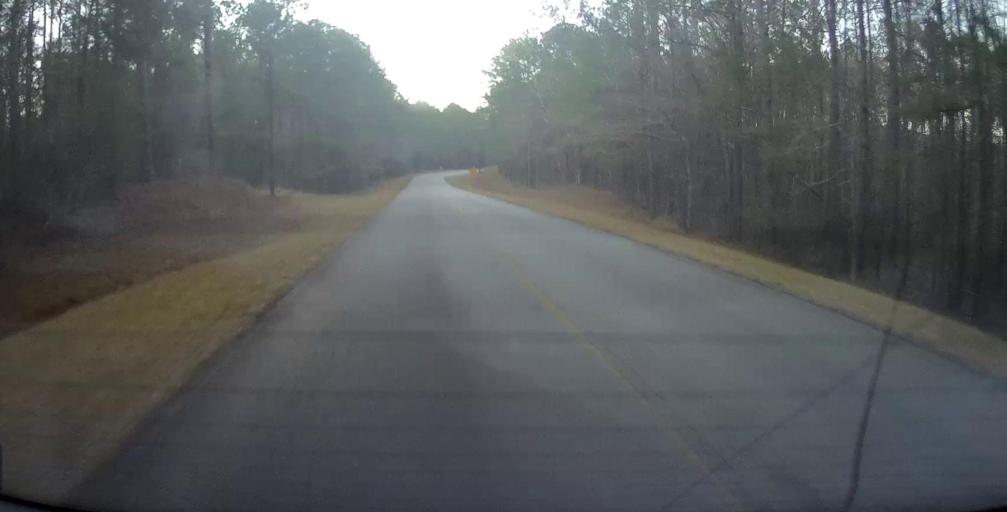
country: US
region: Georgia
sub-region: Harris County
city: Hamilton
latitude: 32.6145
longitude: -84.8525
